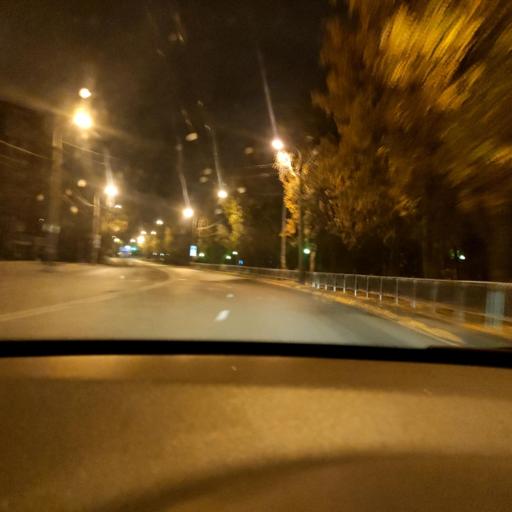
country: RU
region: Samara
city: Samara
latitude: 53.2418
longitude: 50.2280
